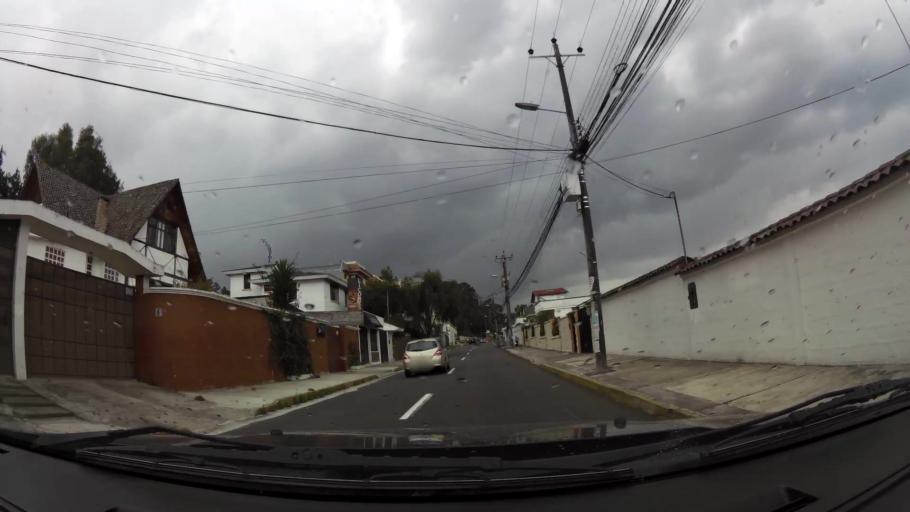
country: EC
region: Pichincha
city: Quito
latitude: -0.1054
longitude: -78.4820
